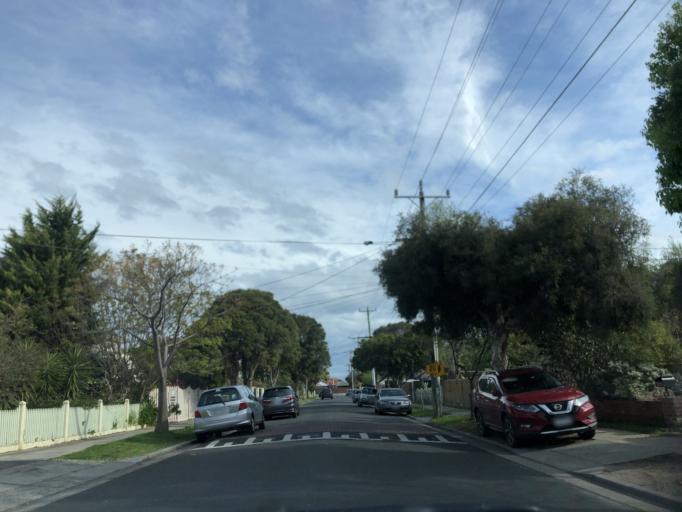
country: AU
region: Victoria
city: Hughesdale
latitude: -37.9119
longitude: 145.0878
